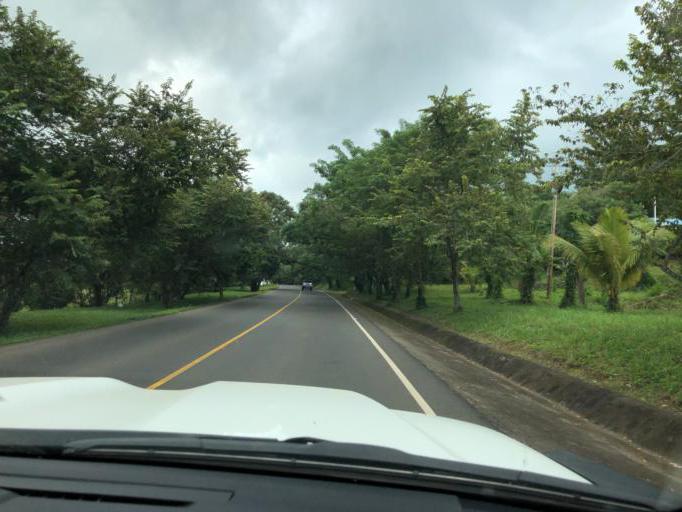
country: NI
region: Chontales
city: Villa Sandino
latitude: 12.0545
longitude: -85.0287
